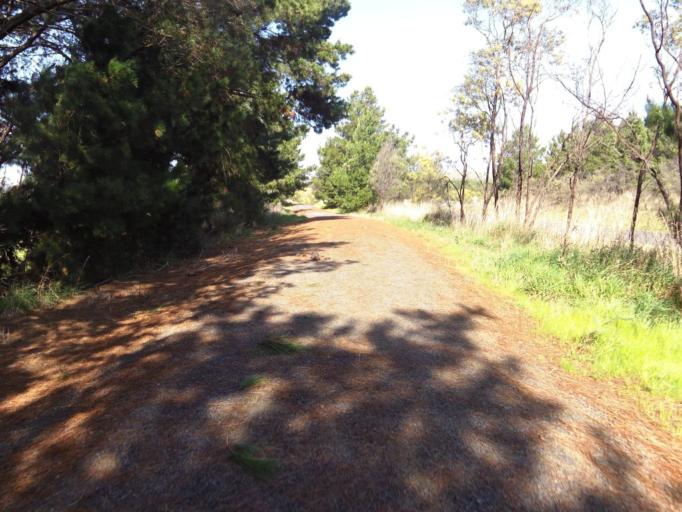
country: AU
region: Victoria
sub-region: Murrindindi
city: Alexandra
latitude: -37.0092
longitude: 145.7536
